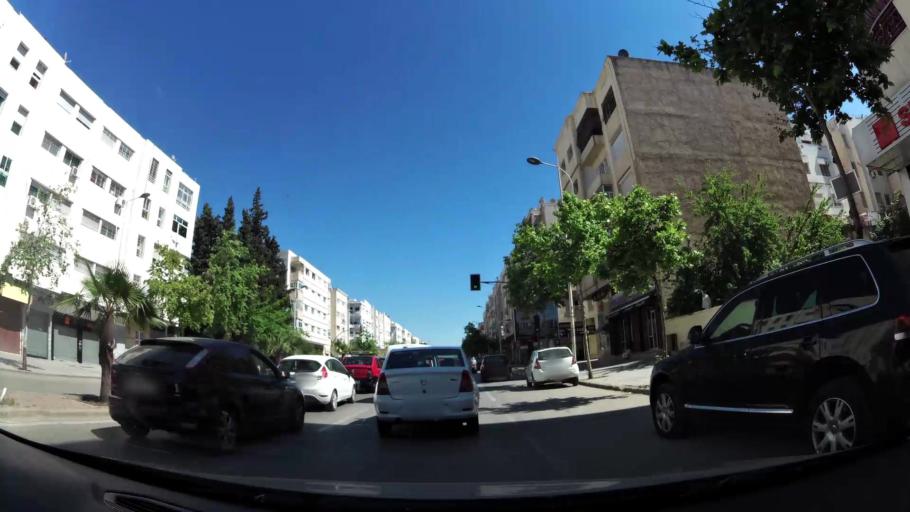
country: MA
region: Fes-Boulemane
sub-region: Fes
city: Fes
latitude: 34.0229
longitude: -4.9889
